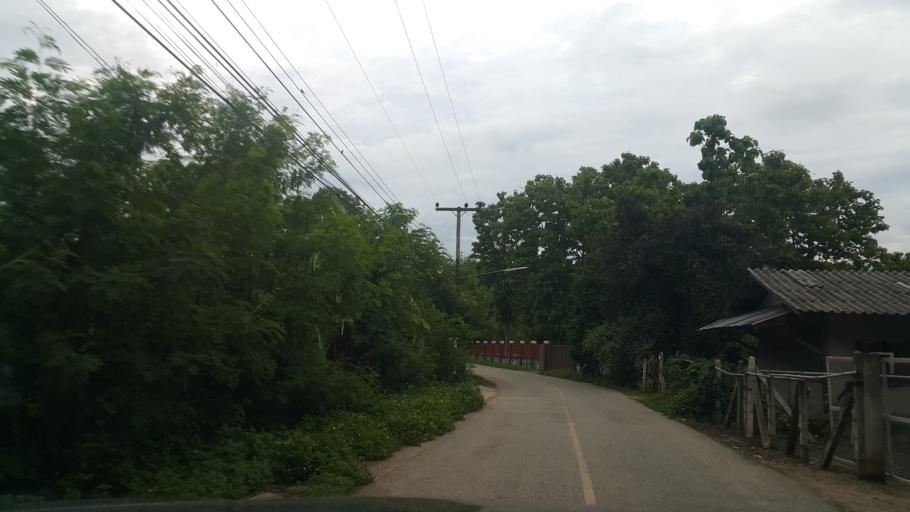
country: TH
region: Chiang Mai
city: Mae On
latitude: 18.7353
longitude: 99.2213
